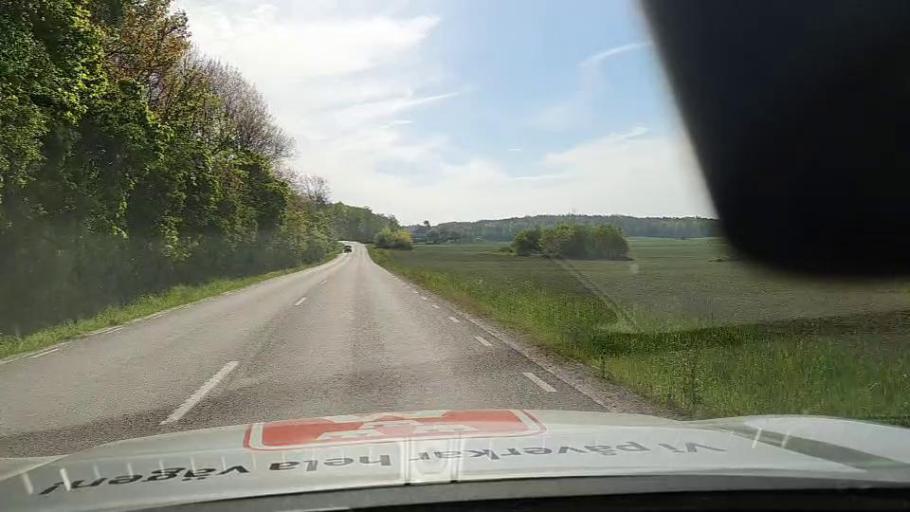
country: SE
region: Soedermanland
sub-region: Eskilstuna Kommun
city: Eskilstuna
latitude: 59.3181
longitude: 16.5804
